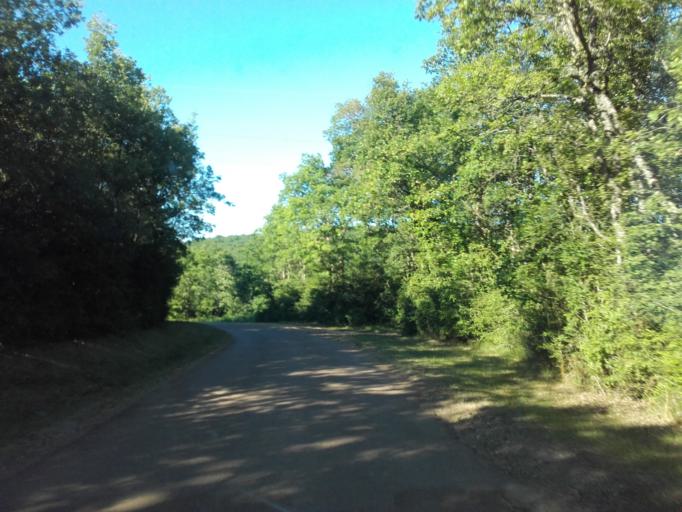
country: FR
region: Bourgogne
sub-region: Departement de Saone-et-Loire
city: Rully
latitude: 46.8455
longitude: 4.7386
